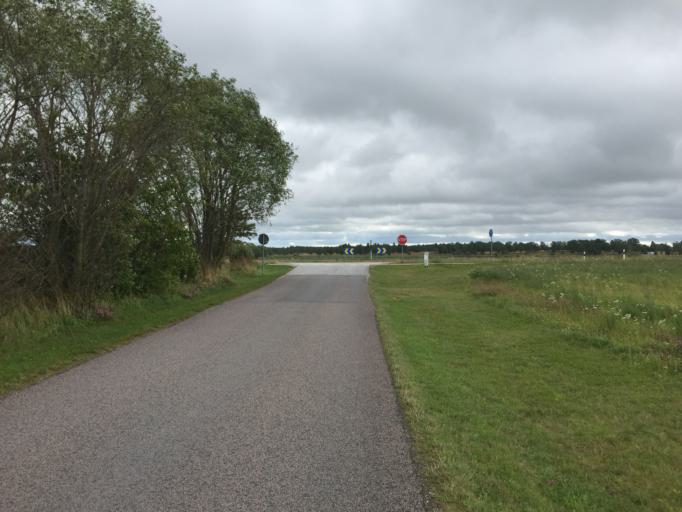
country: SE
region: Gotland
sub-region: Gotland
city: Klintehamn
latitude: 57.4509
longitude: 18.1338
